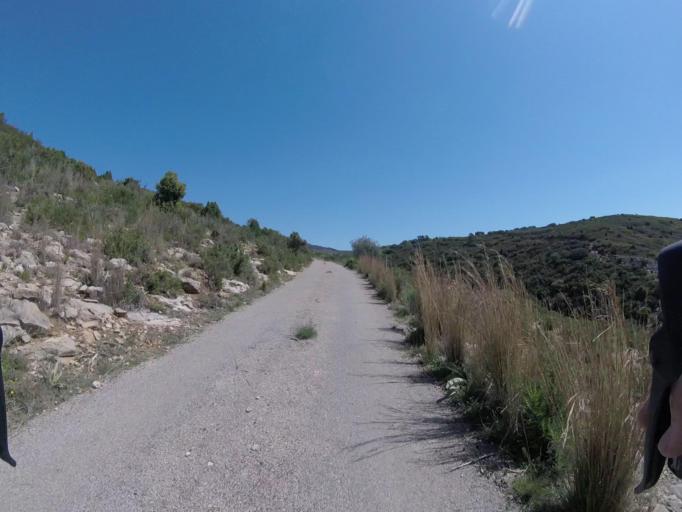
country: ES
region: Valencia
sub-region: Provincia de Castello
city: Sierra-Engarceran
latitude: 40.2525
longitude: -0.0260
